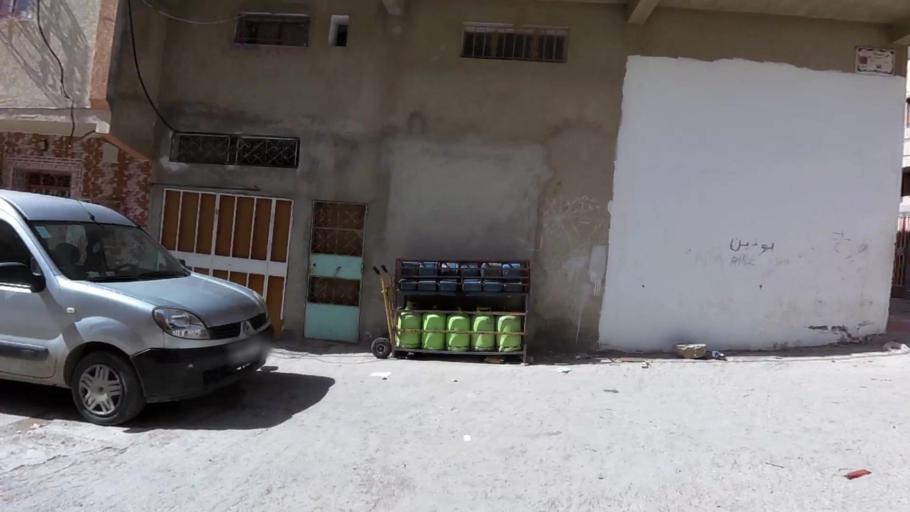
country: MA
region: Tanger-Tetouan
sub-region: Tanger-Assilah
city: Tangier
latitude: 35.7669
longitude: -5.7699
